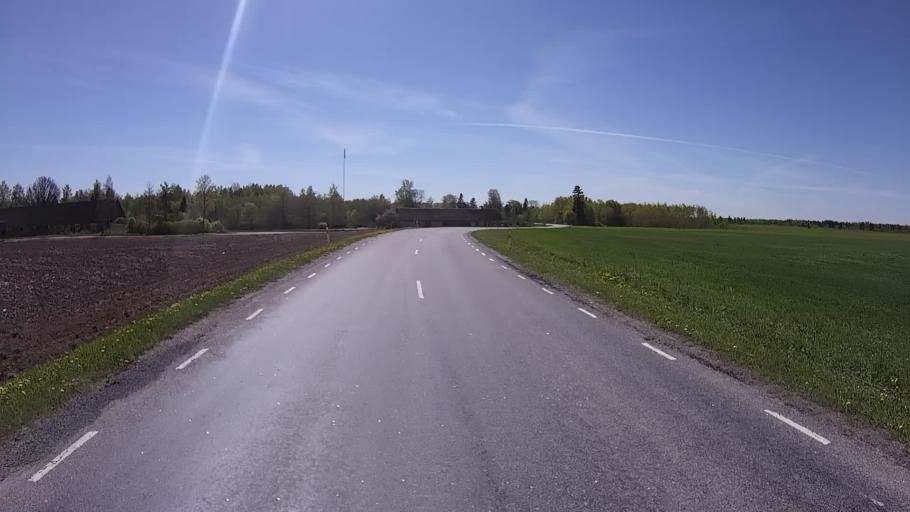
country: EE
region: Harju
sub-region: Rae vald
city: Vaida
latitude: 59.0734
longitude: 25.1624
